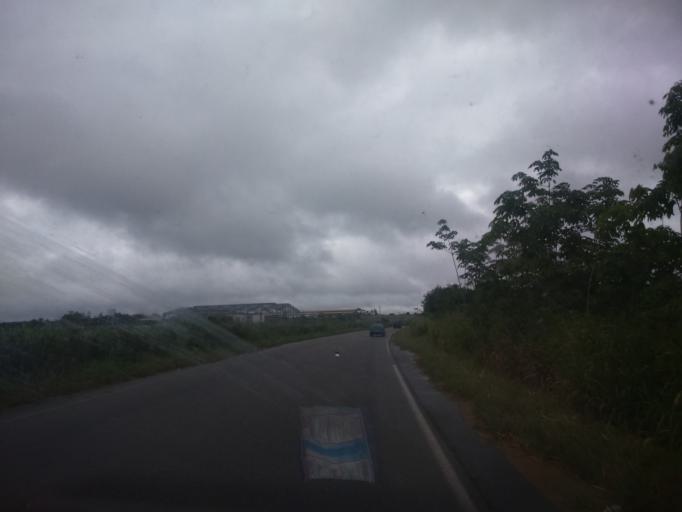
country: CI
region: Sud-Comoe
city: Bonoua
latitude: 5.2784
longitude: -3.5573
